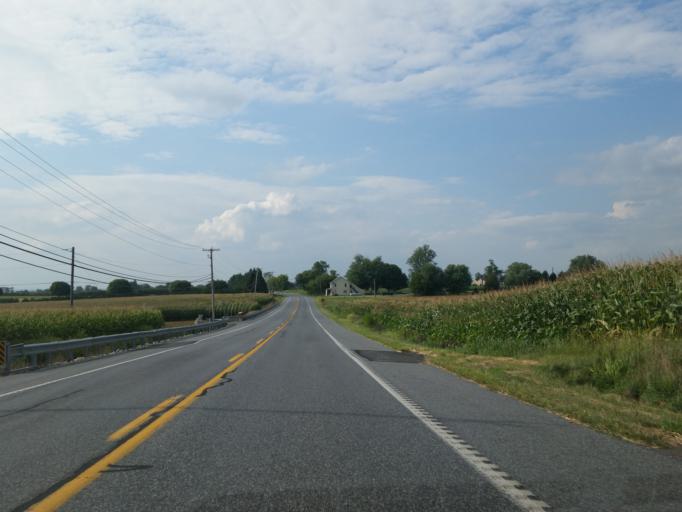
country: US
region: Pennsylvania
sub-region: Lebanon County
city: Annville
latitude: 40.2993
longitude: -76.4932
